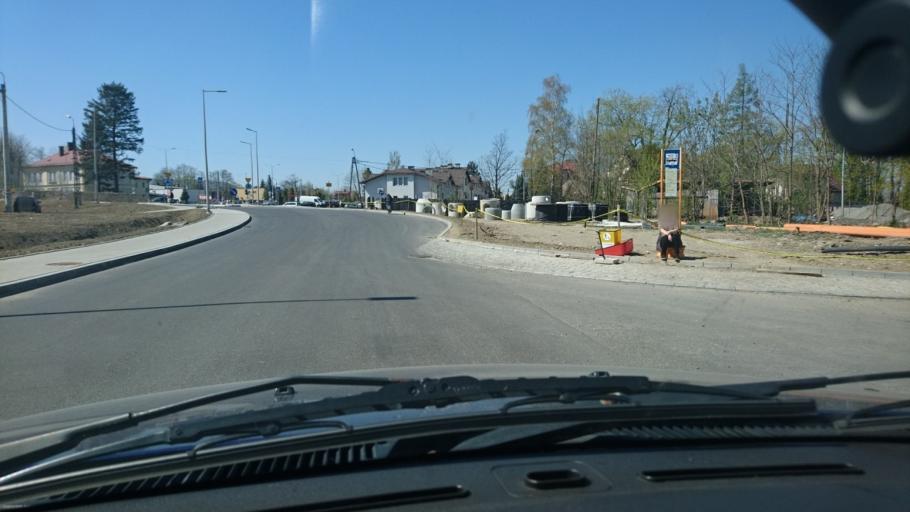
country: PL
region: Silesian Voivodeship
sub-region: Powiat bielski
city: Jaworze
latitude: 49.8086
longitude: 18.9835
